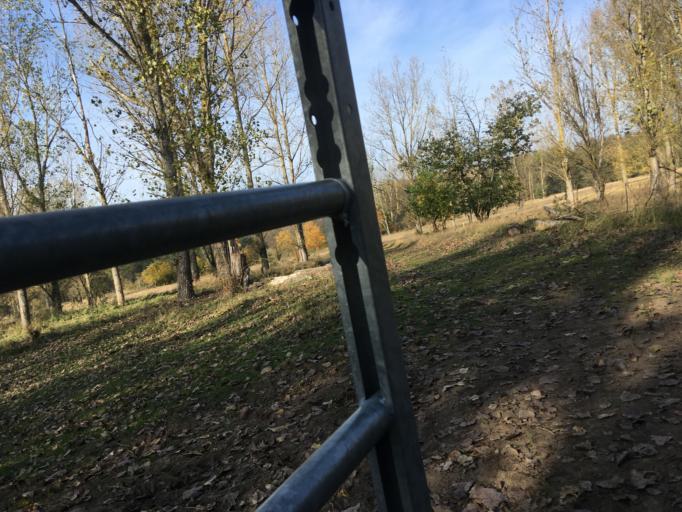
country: DE
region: Berlin
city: Buch
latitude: 52.6722
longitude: 13.4912
